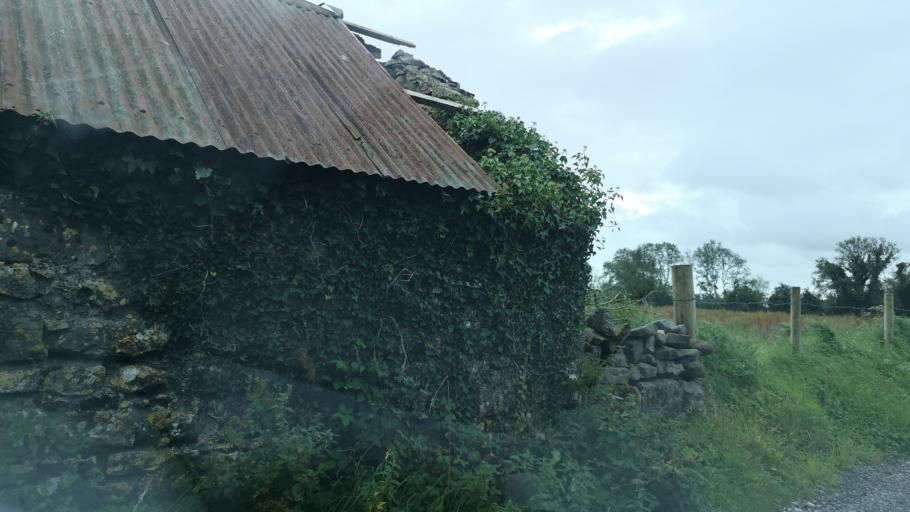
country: IE
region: Connaught
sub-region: County Galway
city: Loughrea
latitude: 53.2949
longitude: -8.6186
